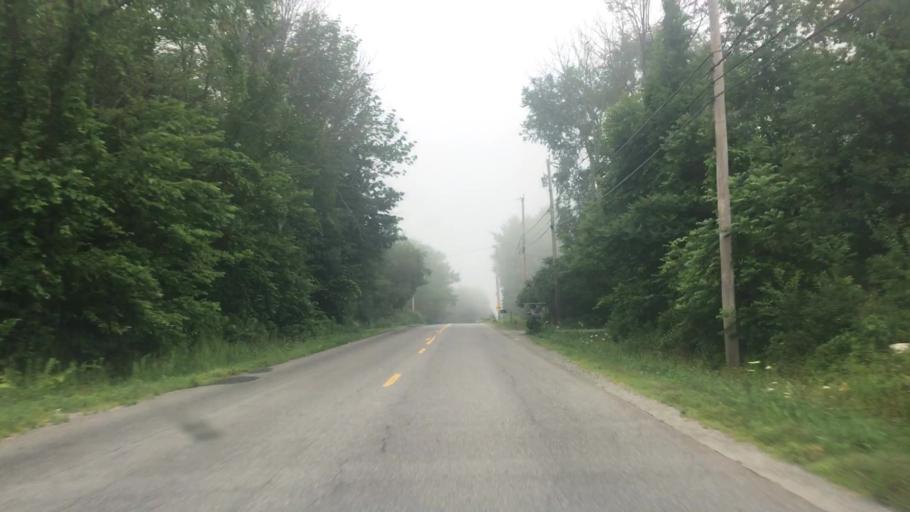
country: US
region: Maine
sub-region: Kennebec County
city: Oakland
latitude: 44.5262
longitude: -69.7256
